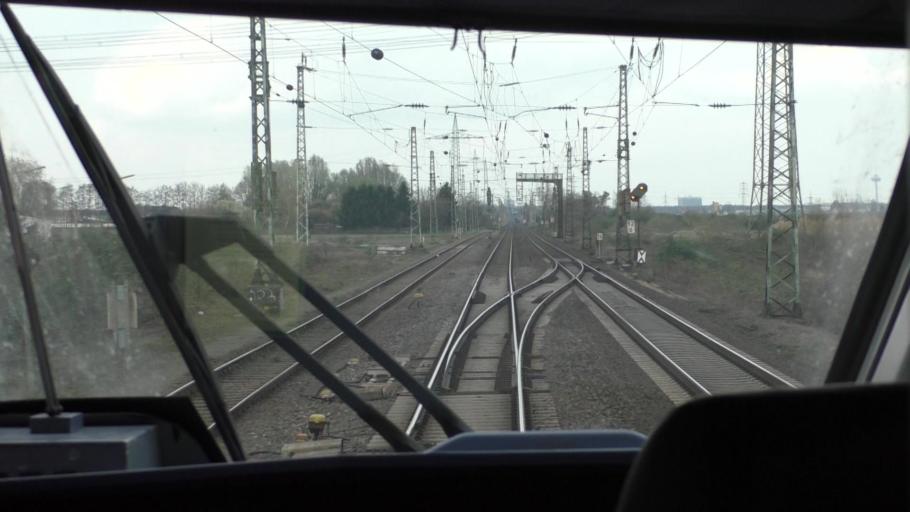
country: DE
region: North Rhine-Westphalia
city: Bruhl
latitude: 50.8452
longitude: 6.9090
